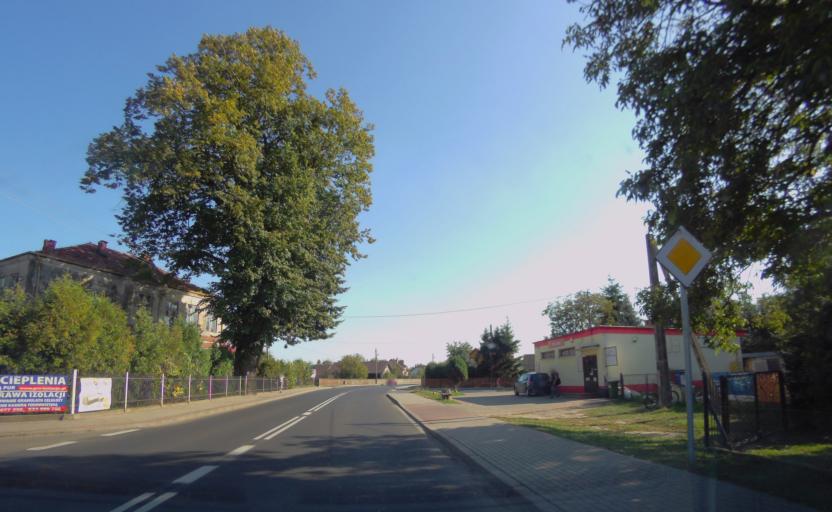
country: PL
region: Subcarpathian Voivodeship
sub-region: Powiat lezajski
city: Stare Miasto
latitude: 50.2861
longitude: 22.4291
